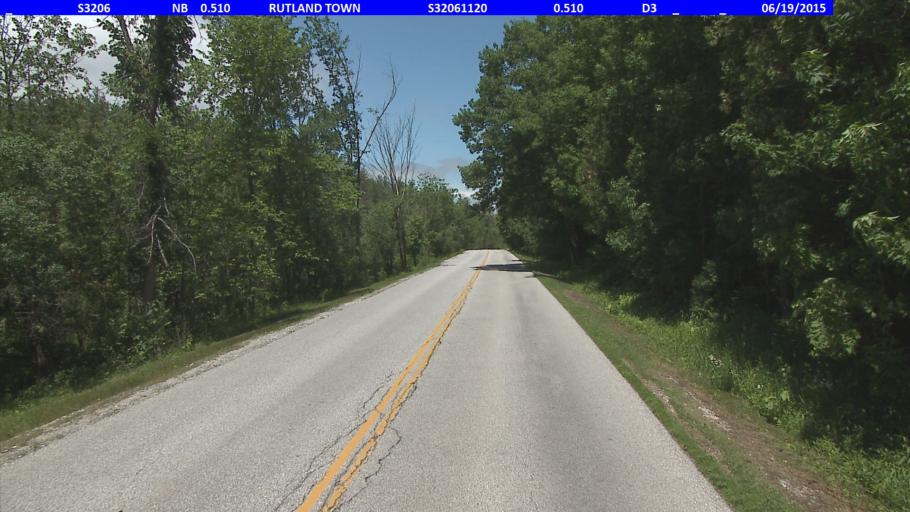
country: US
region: Vermont
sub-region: Rutland County
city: Rutland
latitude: 43.6369
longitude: -72.9908
